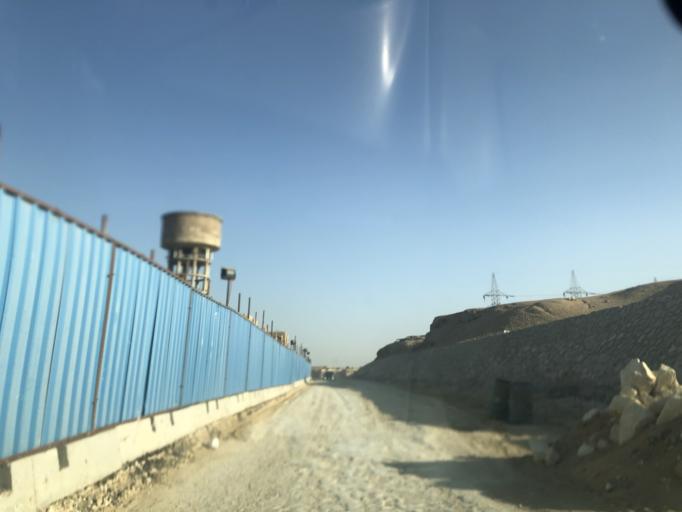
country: EG
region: Al Jizah
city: Al Jizah
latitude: 29.9909
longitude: 31.1106
